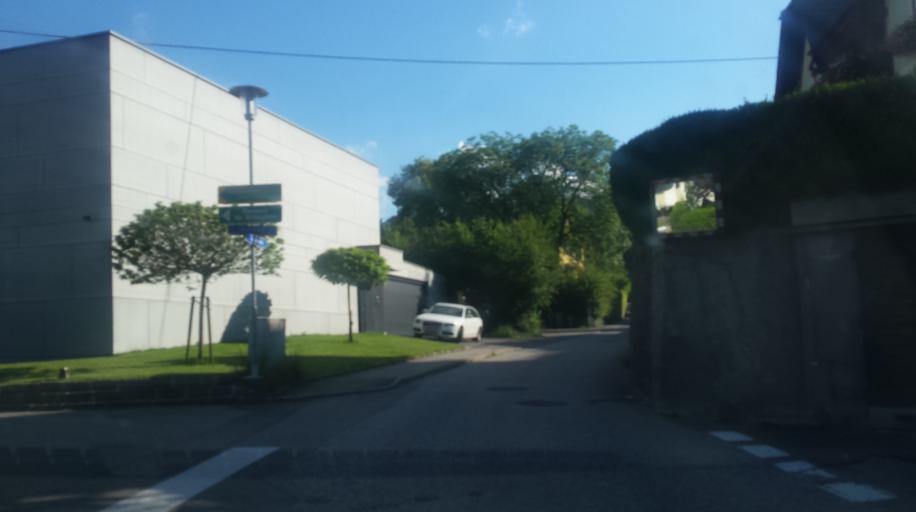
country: AT
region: Upper Austria
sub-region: Politischer Bezirk Gmunden
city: Altmunster
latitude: 47.8973
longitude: 13.7587
